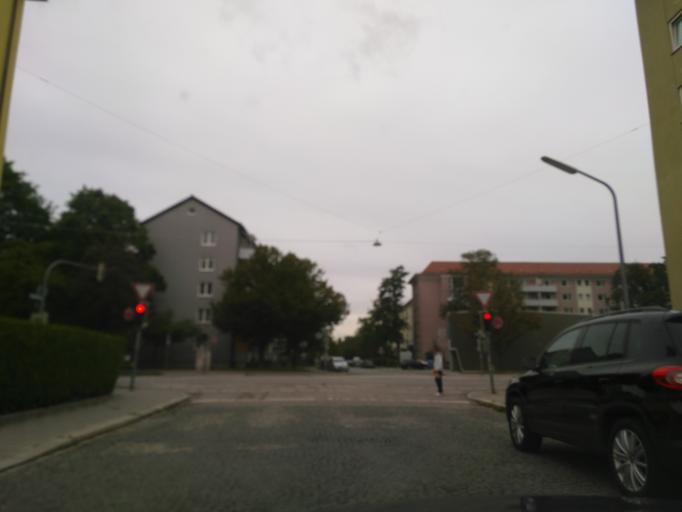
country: DE
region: Bavaria
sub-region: Upper Bavaria
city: Munich
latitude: 48.1051
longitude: 11.5913
